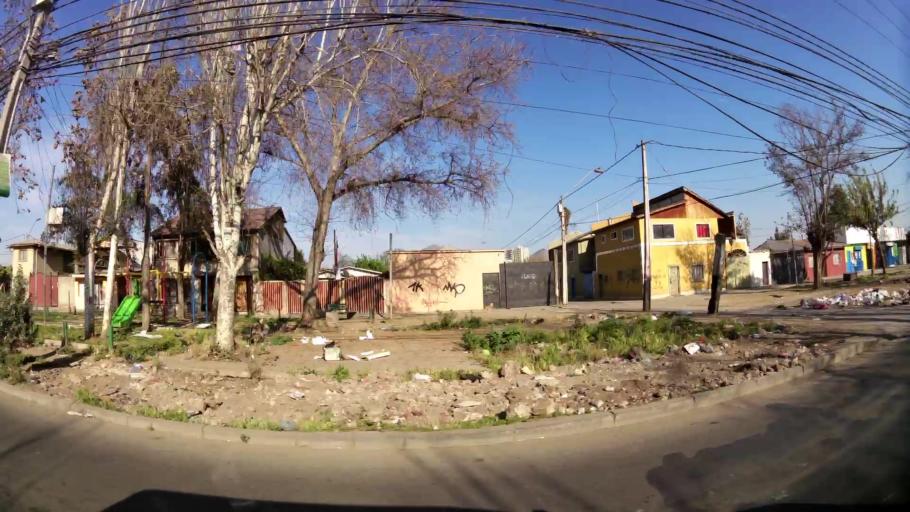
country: CL
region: Santiago Metropolitan
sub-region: Provincia de Santiago
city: Santiago
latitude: -33.3854
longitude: -70.6717
